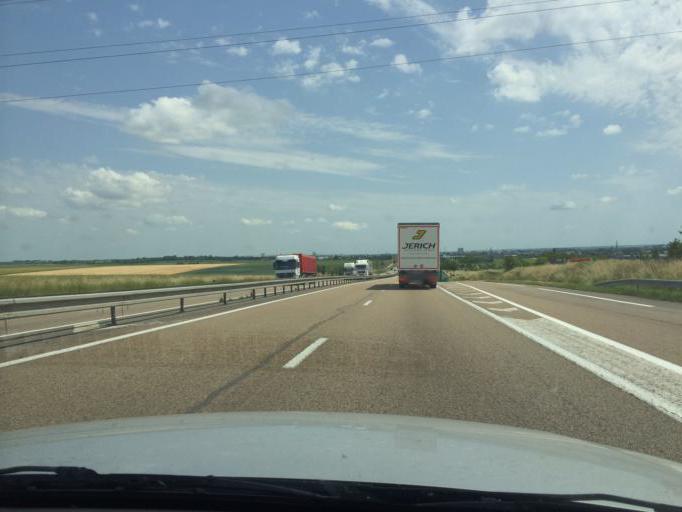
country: FR
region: Champagne-Ardenne
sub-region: Departement de la Marne
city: Fagnieres
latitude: 48.9954
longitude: 4.3422
